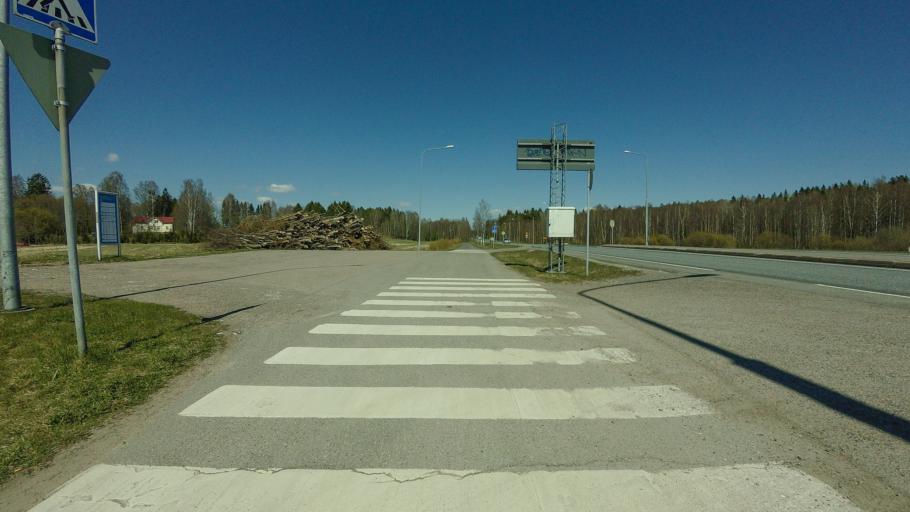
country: FI
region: Uusimaa
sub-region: Helsinki
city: Vantaa
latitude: 60.2338
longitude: 25.1339
